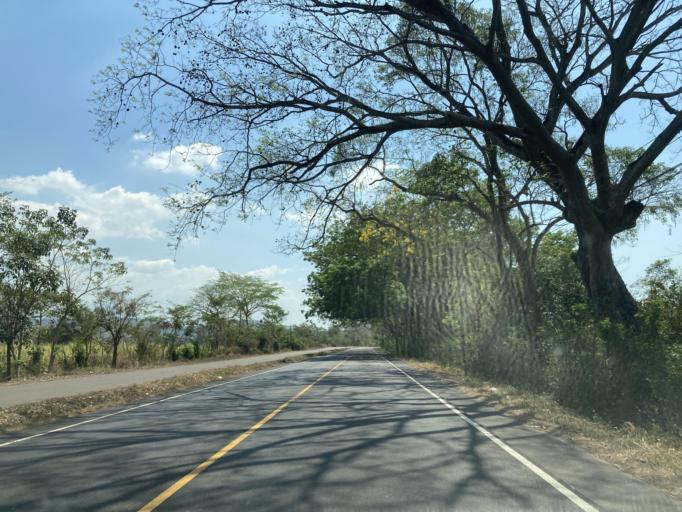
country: GT
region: Escuintla
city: Guanagazapa
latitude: 14.1761
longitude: -90.6826
